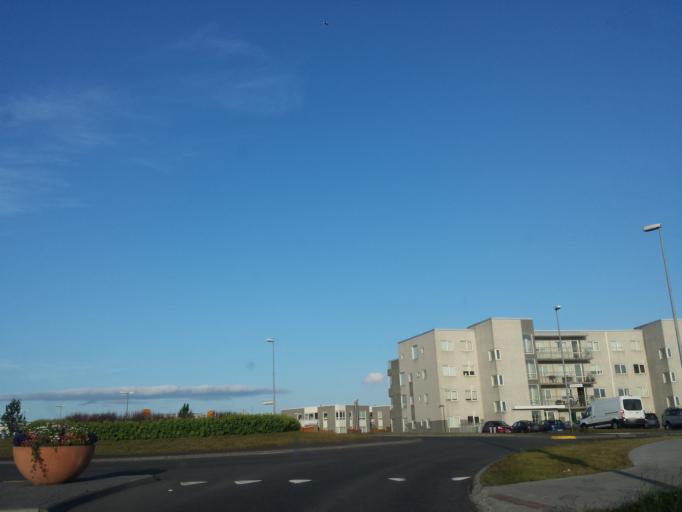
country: IS
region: Capital Region
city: Mosfellsbaer
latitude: 64.1007
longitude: -21.7789
